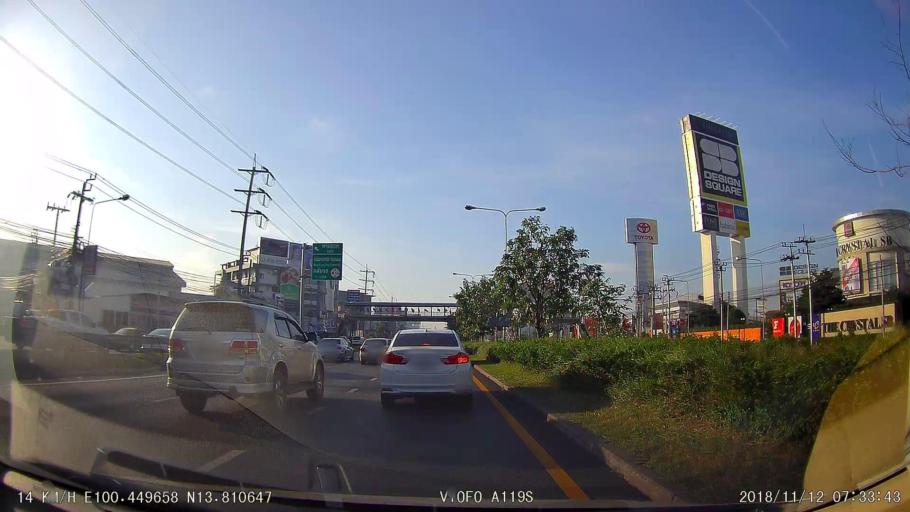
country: TH
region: Nonthaburi
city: Bang Kruai
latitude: 13.8106
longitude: 100.4497
